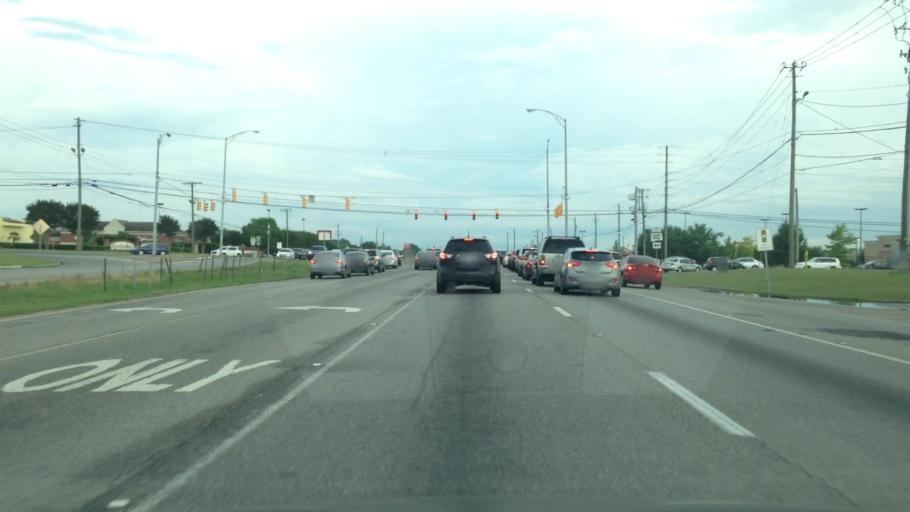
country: US
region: Alabama
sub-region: Montgomery County
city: Pike Road
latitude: 32.3396
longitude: -86.1794
